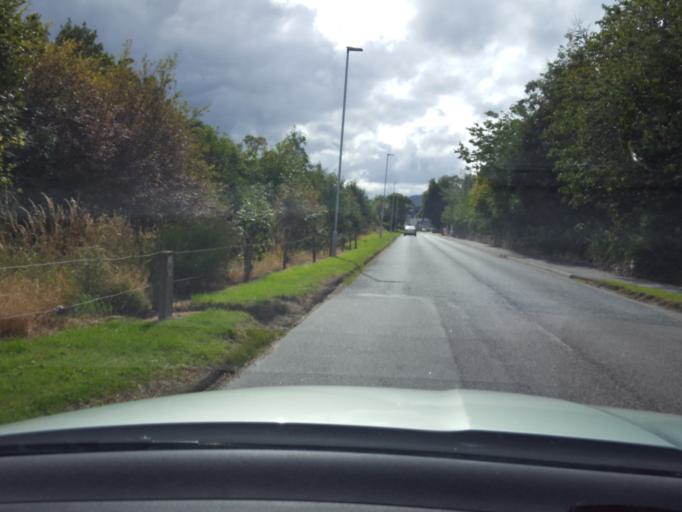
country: GB
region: Scotland
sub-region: Aberdeenshire
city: Ballater
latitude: 57.0503
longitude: -3.0335
